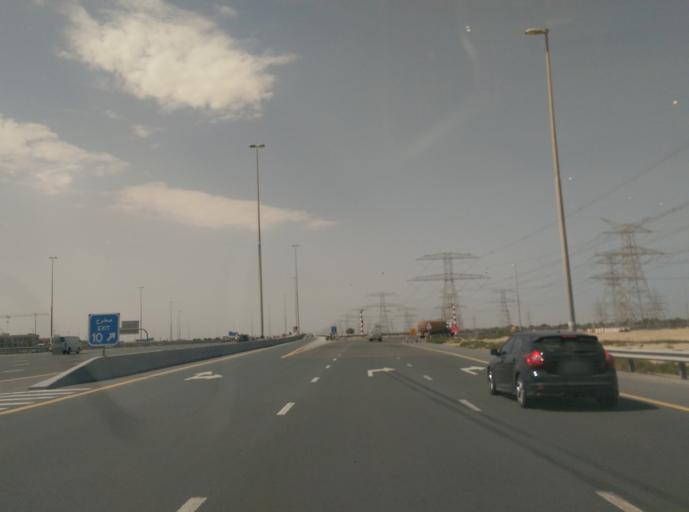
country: AE
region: Dubai
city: Dubai
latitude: 25.0652
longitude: 55.1997
